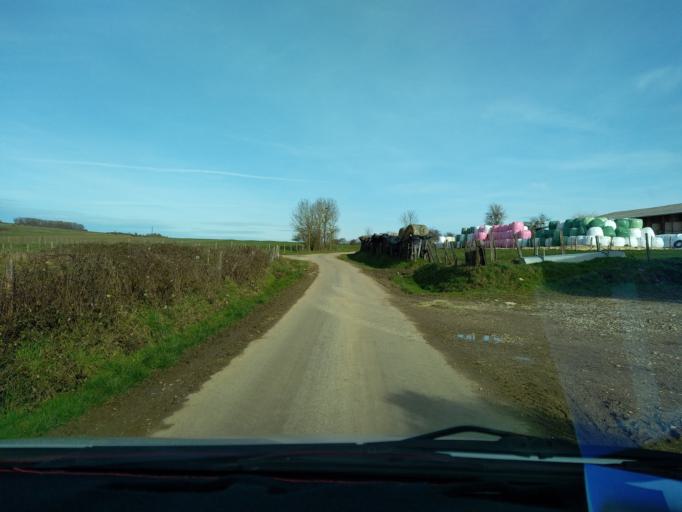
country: FR
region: Franche-Comte
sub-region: Departement de la Haute-Saone
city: Marnay
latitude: 47.2994
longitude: 5.6726
